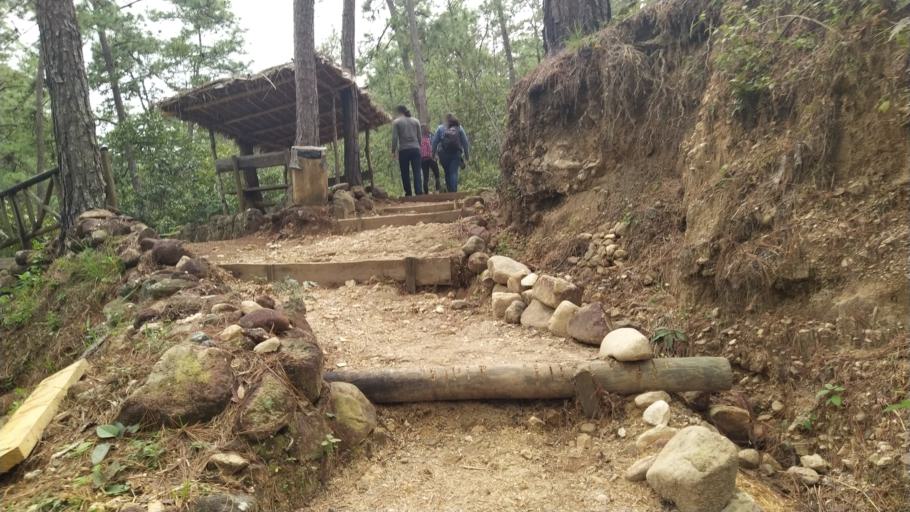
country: GT
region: Chiquimula
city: Esquipulas
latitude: 14.5548
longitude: -89.3192
